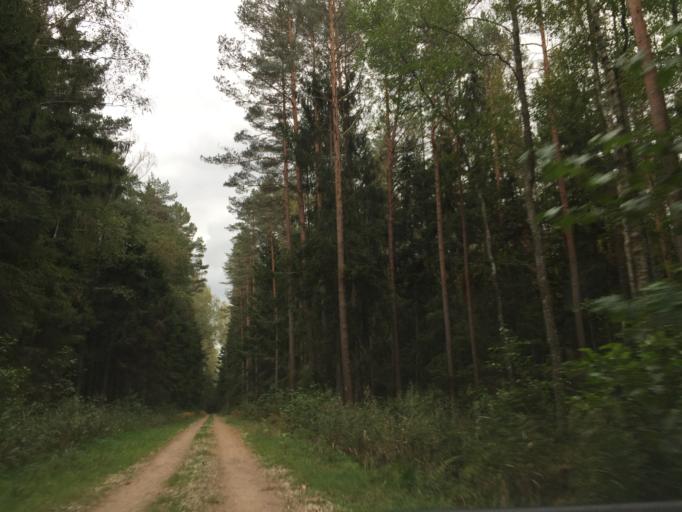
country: LV
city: Tireli
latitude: 56.8894
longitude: 23.5446
